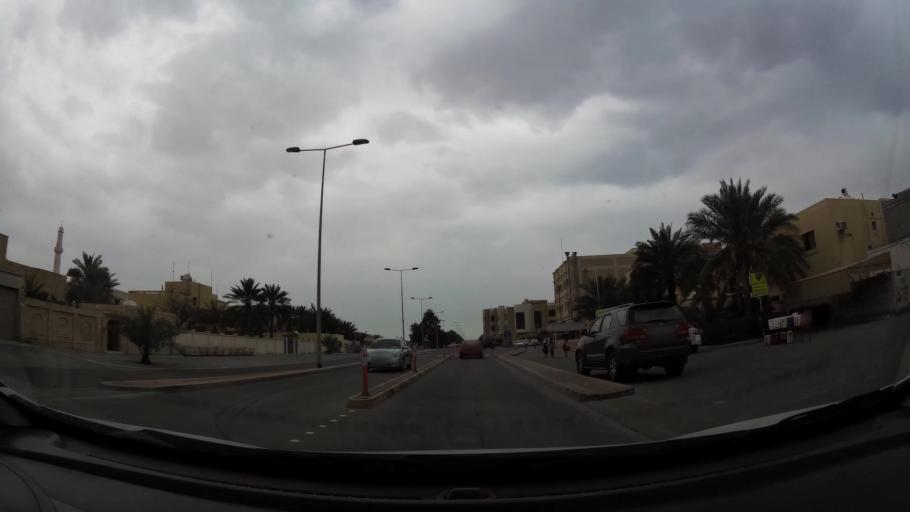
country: BH
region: Central Governorate
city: Dar Kulayb
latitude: 26.0477
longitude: 50.4885
